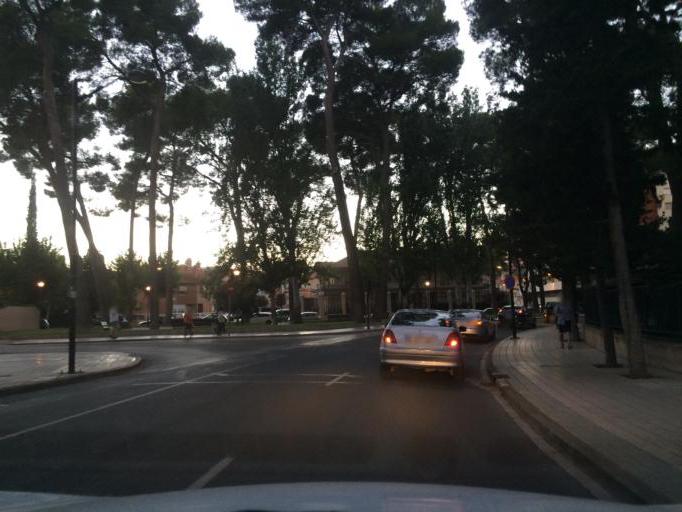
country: ES
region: Castille-La Mancha
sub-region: Provincia de Albacete
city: Albacete
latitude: 38.9856
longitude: -1.8583
